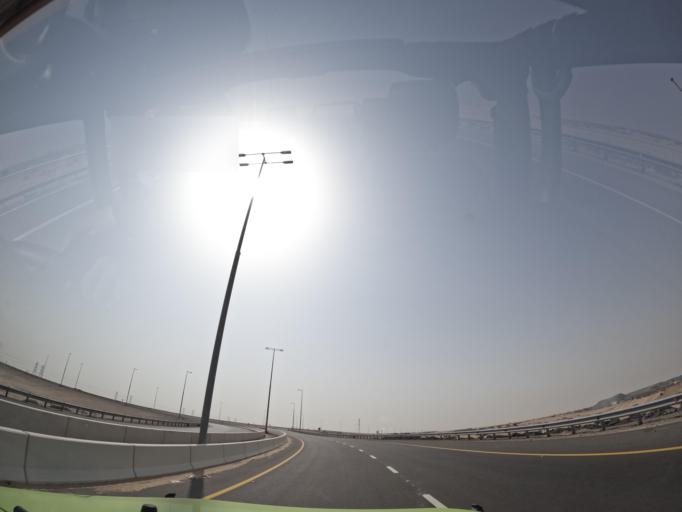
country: AE
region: Dubai
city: Dubai
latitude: 24.7890
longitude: 55.0762
